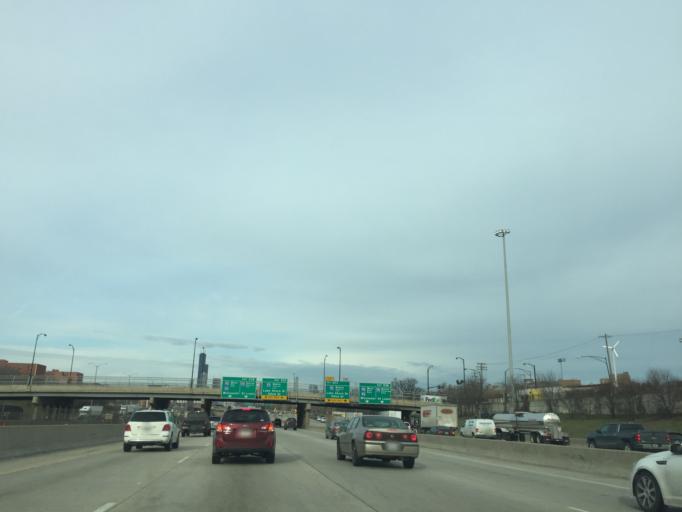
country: US
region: Illinois
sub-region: Cook County
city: Chicago
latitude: 41.8369
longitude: -87.6307
